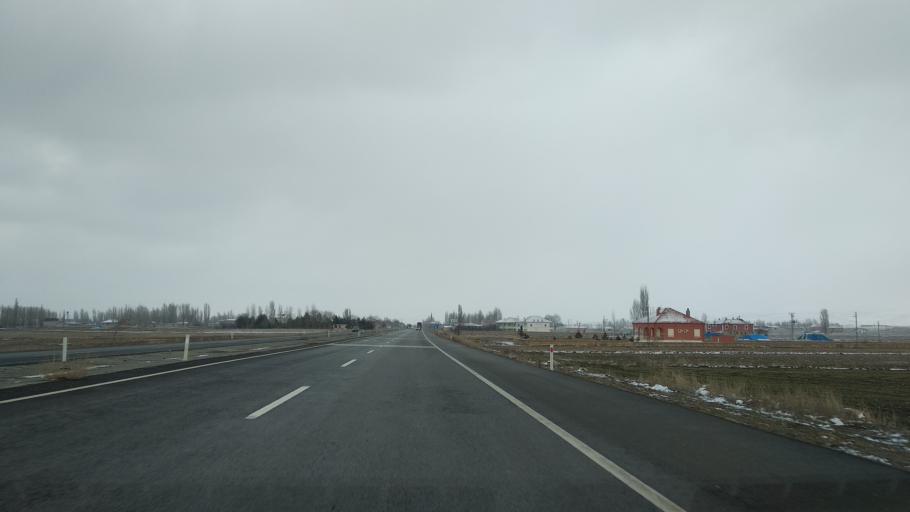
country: TR
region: Kayseri
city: Elbasi
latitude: 38.6422
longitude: 35.9237
